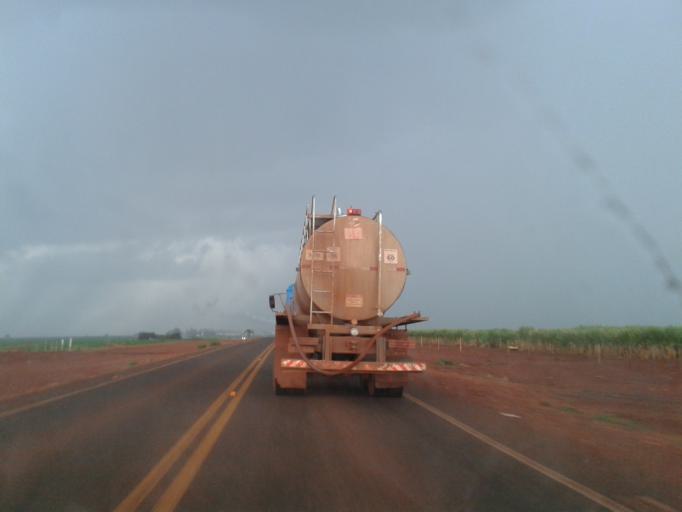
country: BR
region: Goias
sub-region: Quirinopolis
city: Quirinopolis
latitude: -18.5703
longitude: -50.4381
